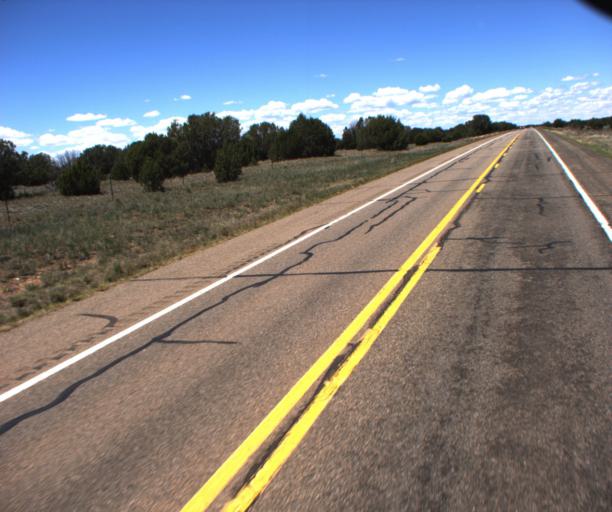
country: US
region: Arizona
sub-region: Yavapai County
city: Paulden
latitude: 35.1448
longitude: -112.4462
